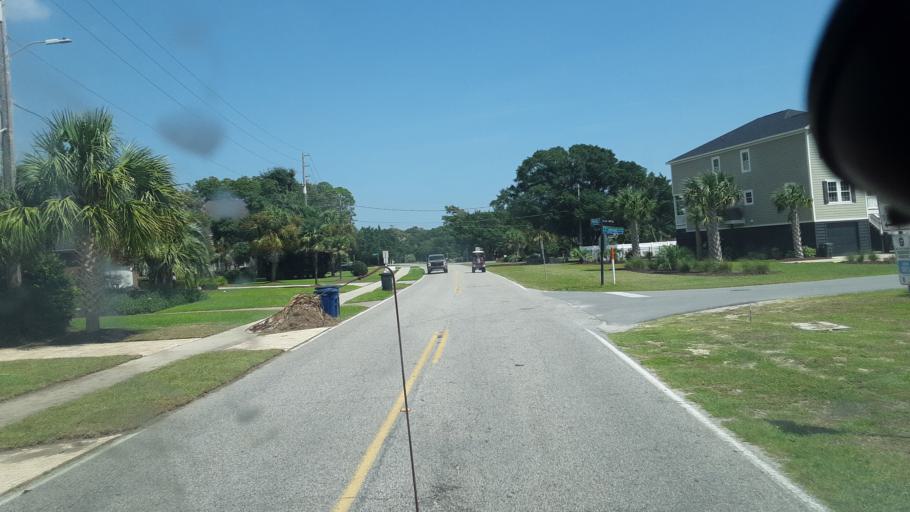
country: US
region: South Carolina
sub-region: Horry County
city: North Myrtle Beach
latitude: 33.8233
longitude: -78.6654
